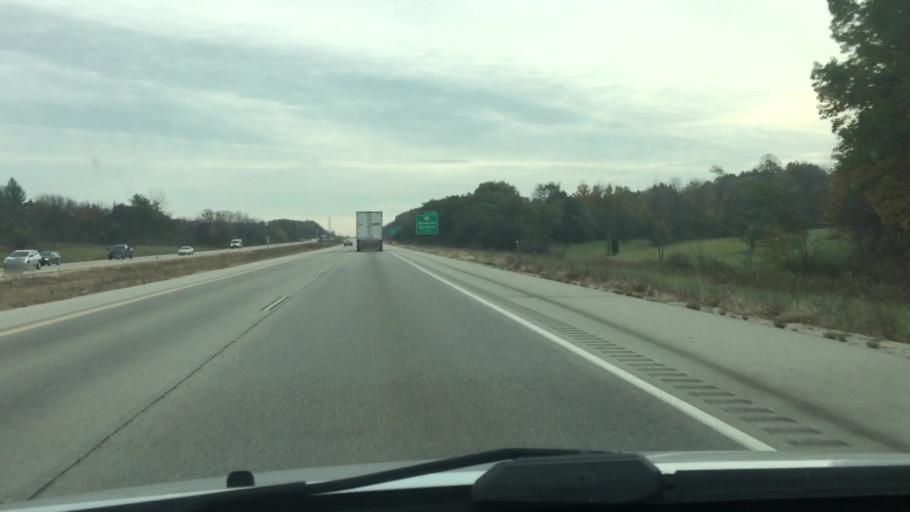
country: US
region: Wisconsin
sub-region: Waukesha County
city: Big Bend
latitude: 42.9035
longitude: -88.2433
